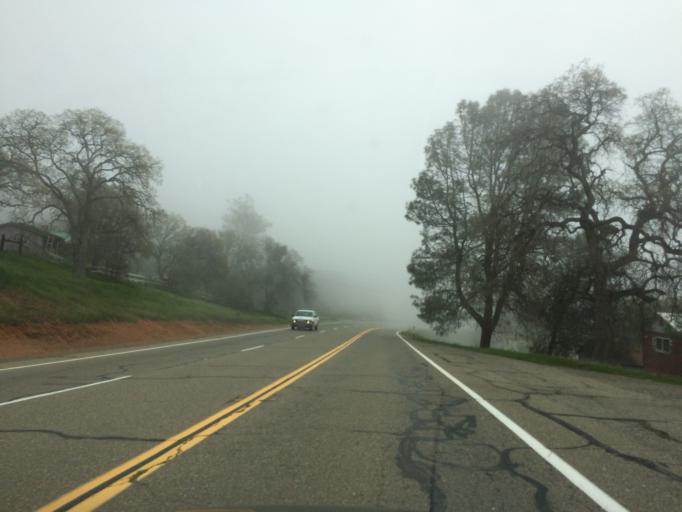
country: US
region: California
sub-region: Mariposa County
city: Mariposa
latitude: 37.4663
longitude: -120.0741
